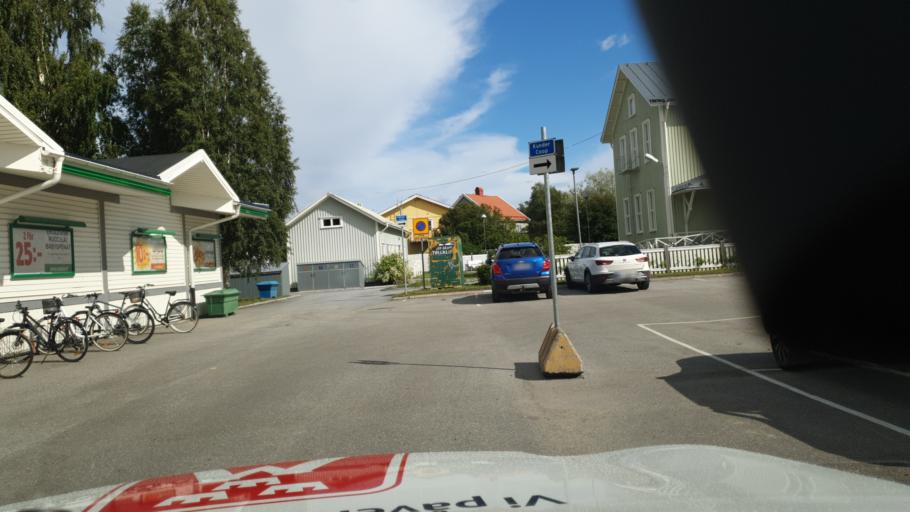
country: SE
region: Vaesterbotten
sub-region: Umea Kommun
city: Roback
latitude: 63.8334
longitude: 20.2170
